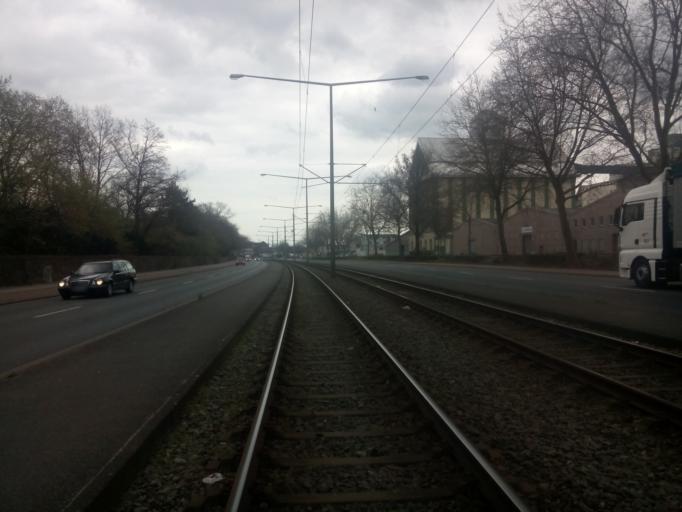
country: DE
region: Bremen
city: Bremen
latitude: 53.1036
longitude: 8.7701
